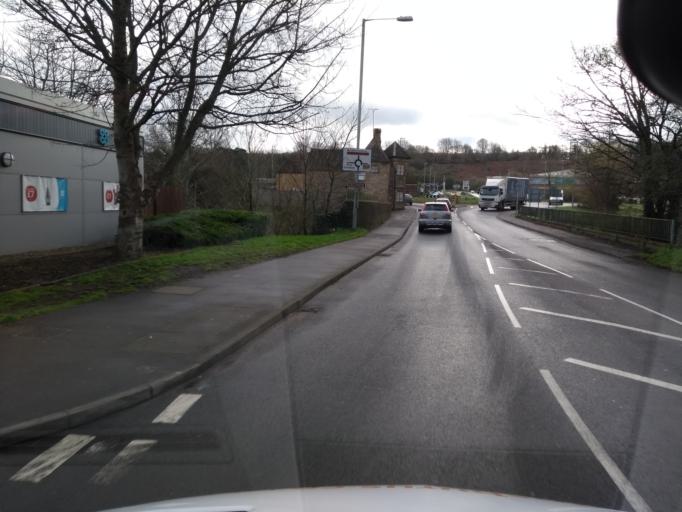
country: GB
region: England
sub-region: Somerset
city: Yeovil
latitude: 50.9422
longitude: -2.6093
